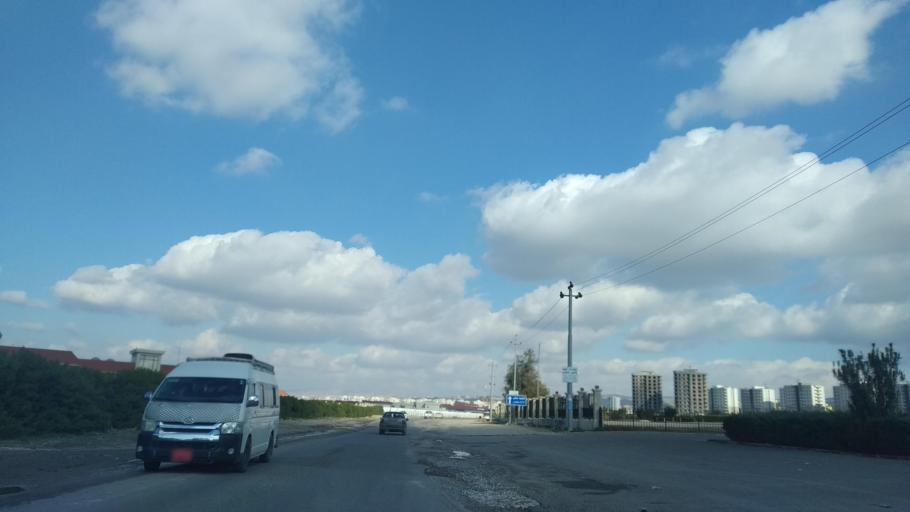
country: IQ
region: Arbil
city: Erbil
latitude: 36.2093
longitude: 44.1340
